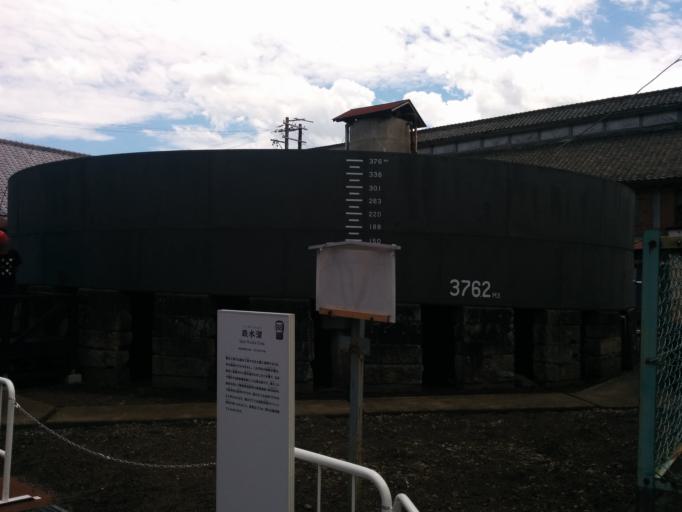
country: JP
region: Gunma
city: Tomioka
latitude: 36.2556
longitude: 138.8869
